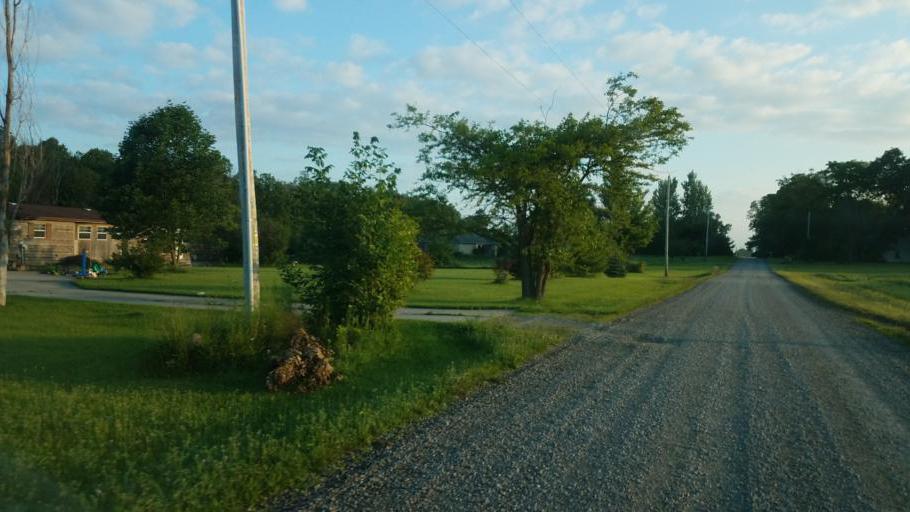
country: US
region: Ohio
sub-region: Morrow County
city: Mount Gilead
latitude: 40.5402
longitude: -82.7012
